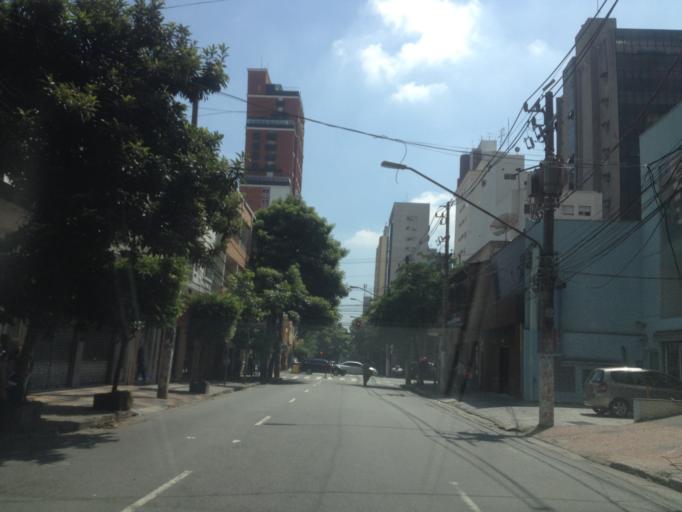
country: BR
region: Sao Paulo
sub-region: Sao Paulo
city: Sao Paulo
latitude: -23.5838
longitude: -46.6758
